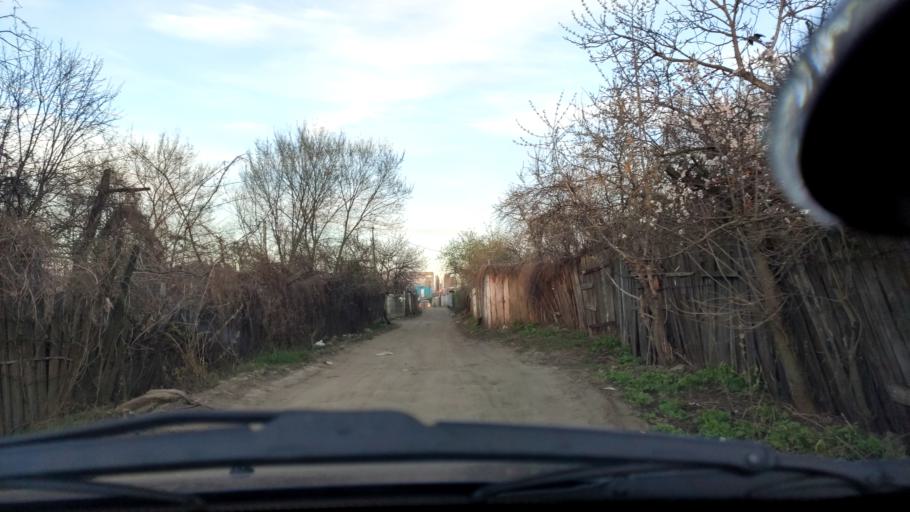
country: RU
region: Voronezj
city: Maslovka
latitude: 51.5977
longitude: 39.2302
